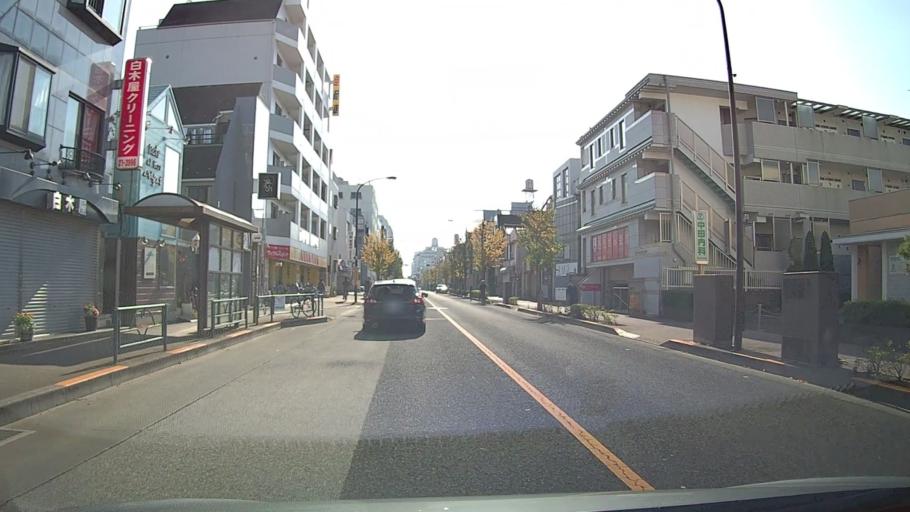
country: JP
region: Tokyo
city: Musashino
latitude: 35.7120
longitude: 139.5818
